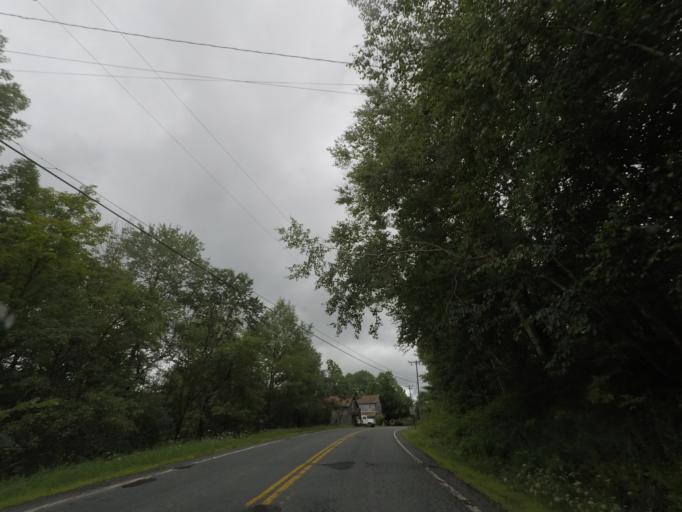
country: US
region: New York
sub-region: Rensselaer County
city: Poestenkill
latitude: 42.6835
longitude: -73.4942
